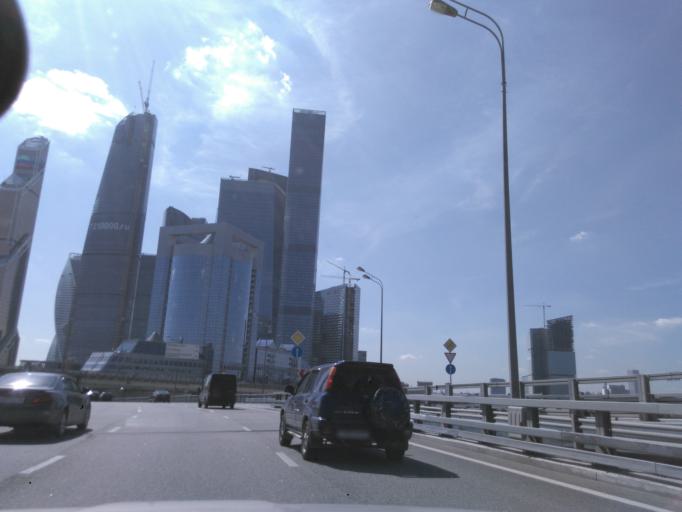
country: RU
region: Moskovskaya
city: Presnenskiy
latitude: 55.7544
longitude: 37.5289
